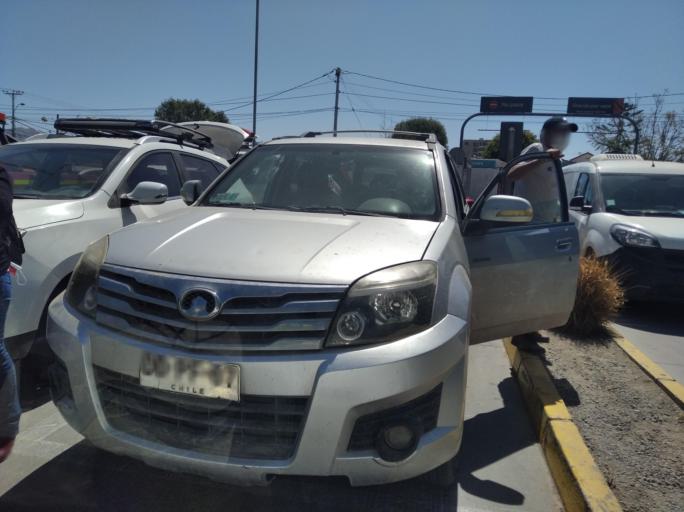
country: CL
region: Atacama
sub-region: Provincia de Copiapo
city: Copiapo
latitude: -27.3975
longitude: -70.2940
